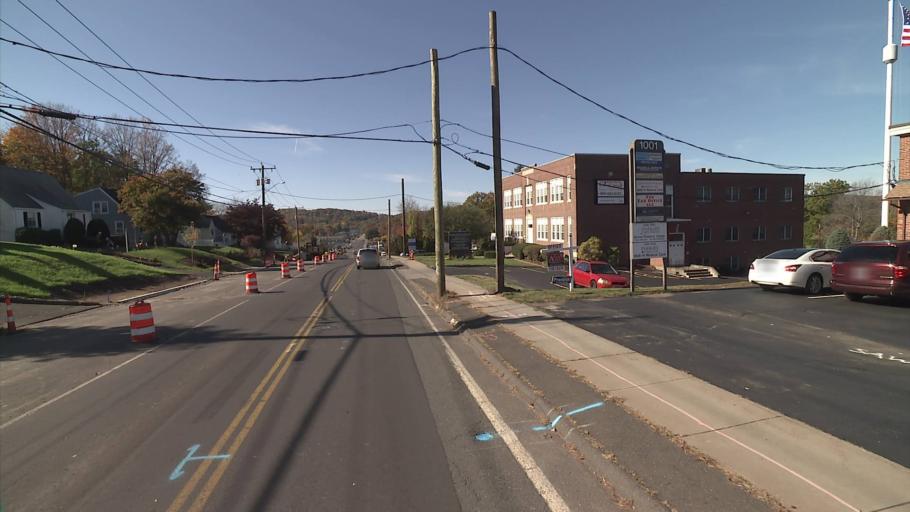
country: US
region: Connecticut
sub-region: Hartford County
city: Bristol
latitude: 41.6951
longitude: -72.9104
